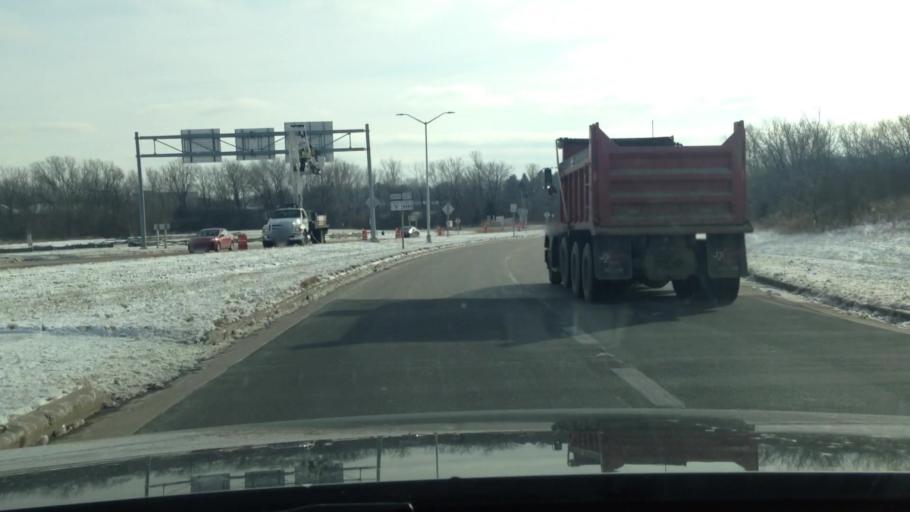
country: US
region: Wisconsin
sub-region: Waukesha County
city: Muskego
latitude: 42.9321
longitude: -88.1592
